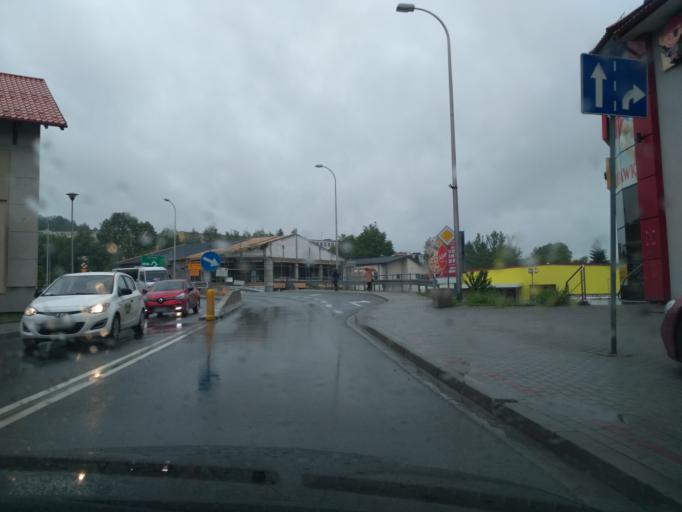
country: PL
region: Lesser Poland Voivodeship
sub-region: Powiat gorlicki
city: Gorlice
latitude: 49.6612
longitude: 21.1592
